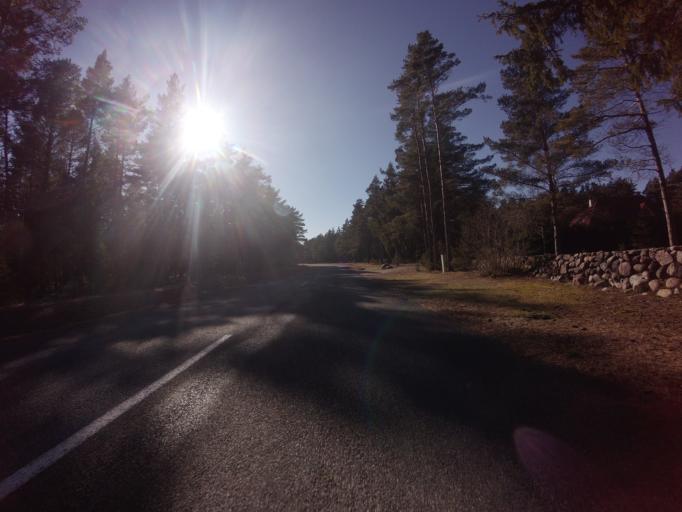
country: EE
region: Saare
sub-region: Kuressaare linn
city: Kuressaare
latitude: 58.5166
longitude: 22.3250
